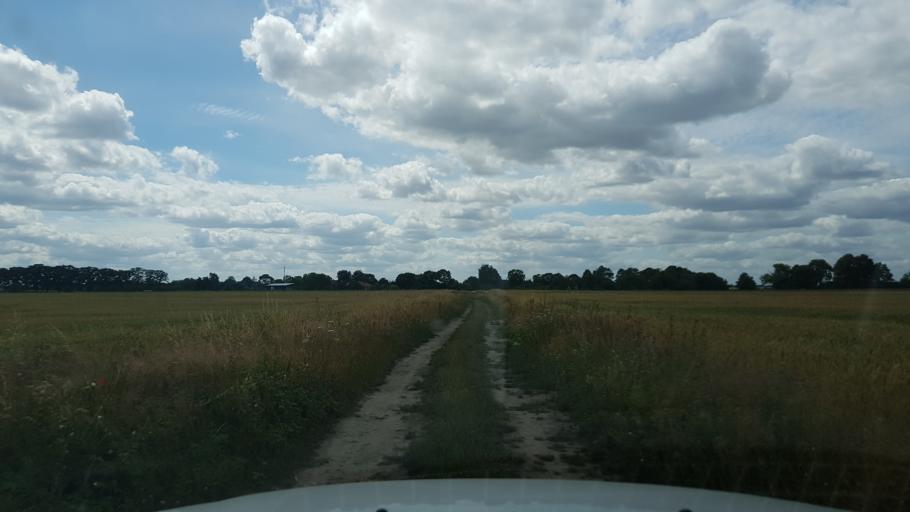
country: PL
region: West Pomeranian Voivodeship
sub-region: Powiat pyrzycki
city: Lipiany
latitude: 52.9623
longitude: 14.9726
